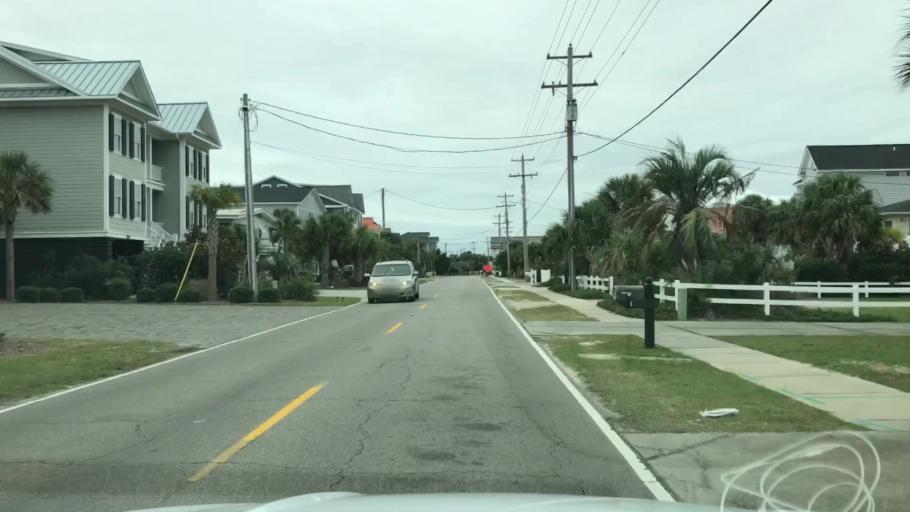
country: US
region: South Carolina
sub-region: Georgetown County
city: Murrells Inlet
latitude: 33.5559
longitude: -79.0162
